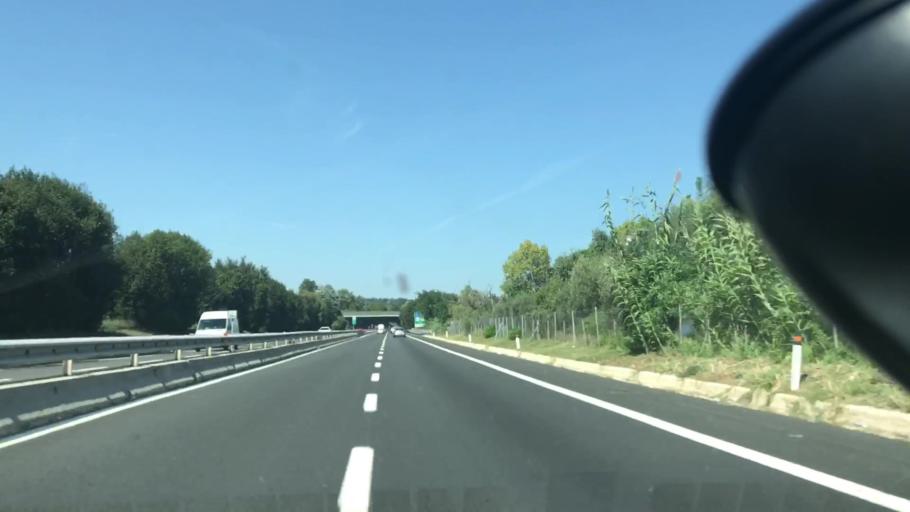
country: IT
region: Abruzzo
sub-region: Provincia di Chieti
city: Miglianico
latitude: 42.3798
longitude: 14.2932
